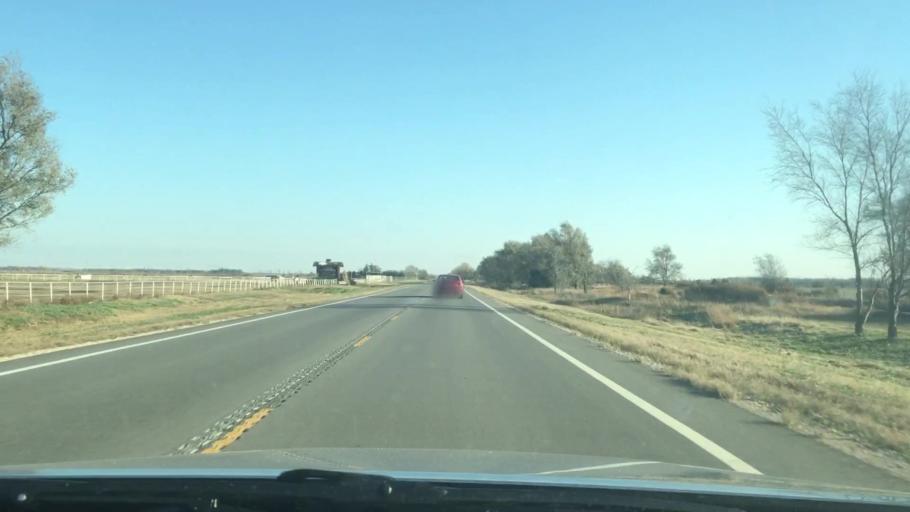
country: US
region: Kansas
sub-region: Reno County
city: Nickerson
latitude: 38.1416
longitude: -98.0753
